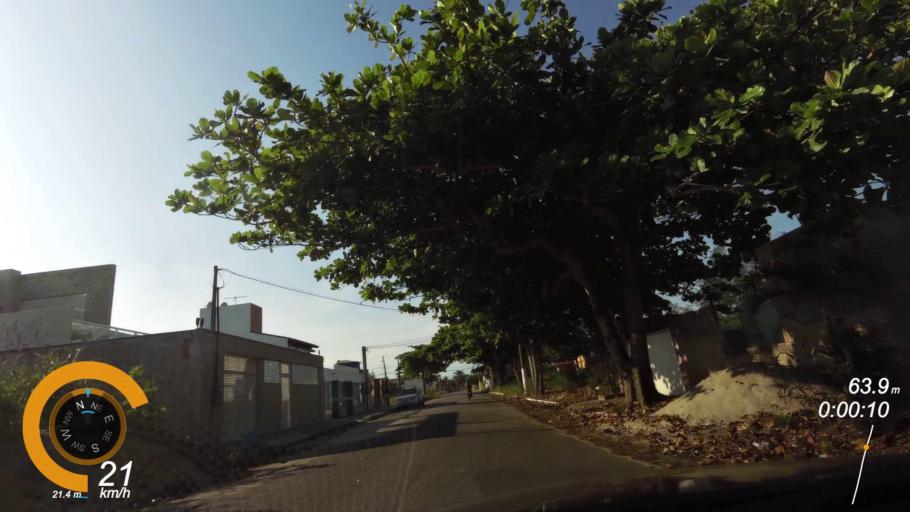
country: BR
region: Espirito Santo
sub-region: Vila Velha
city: Vila Velha
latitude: -20.4857
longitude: -40.3498
